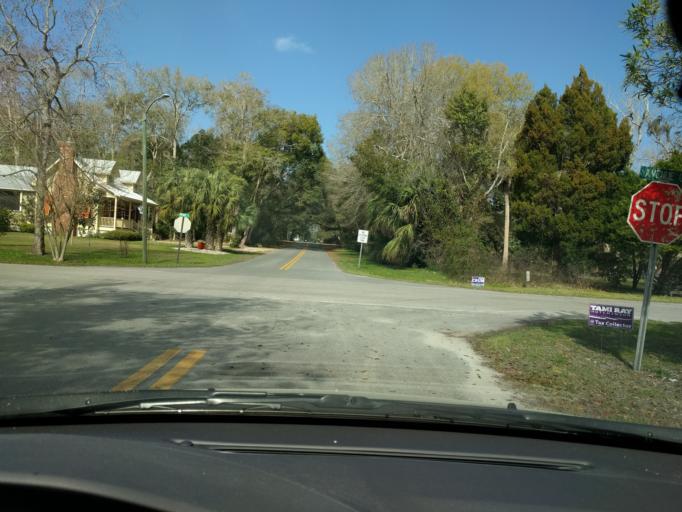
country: US
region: Florida
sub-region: Franklin County
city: Apalachicola
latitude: 29.7265
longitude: -84.9891
